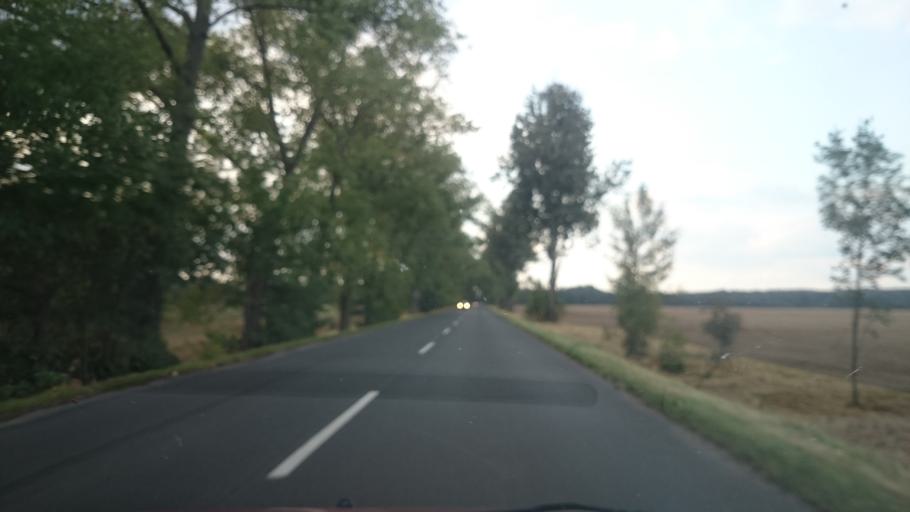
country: PL
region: Opole Voivodeship
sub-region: Powiat nyski
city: Glucholazy
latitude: 50.3571
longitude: 17.3786
